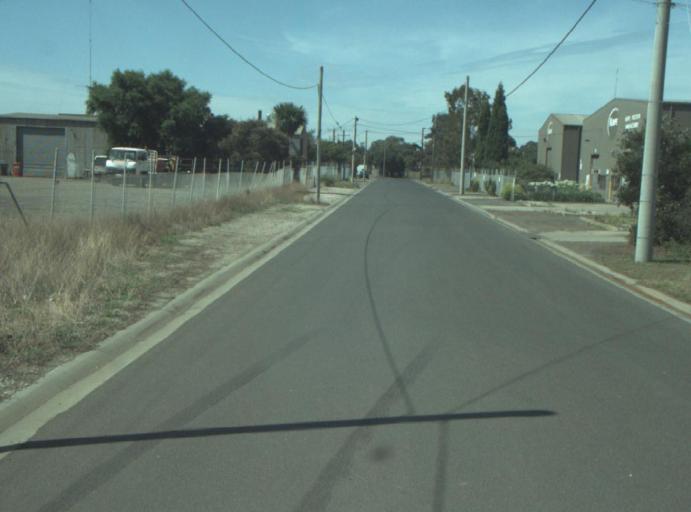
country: AU
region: Victoria
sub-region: Greater Geelong
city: East Geelong
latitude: -38.1671
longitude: 144.4134
